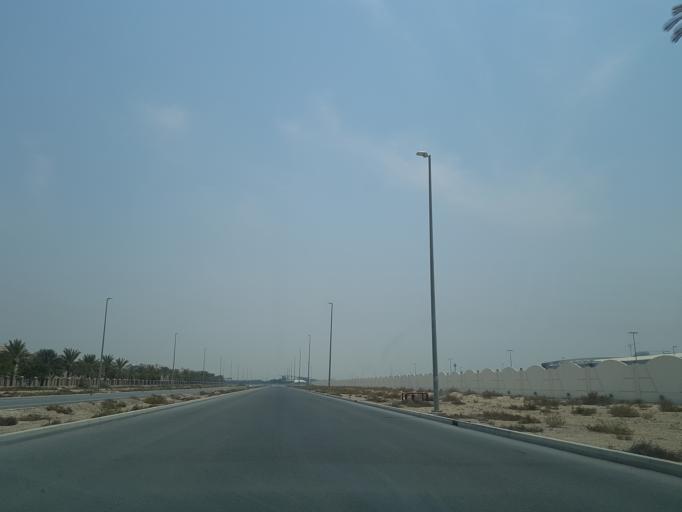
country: AE
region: Dubai
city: Dubai
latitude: 25.0353
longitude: 55.2474
